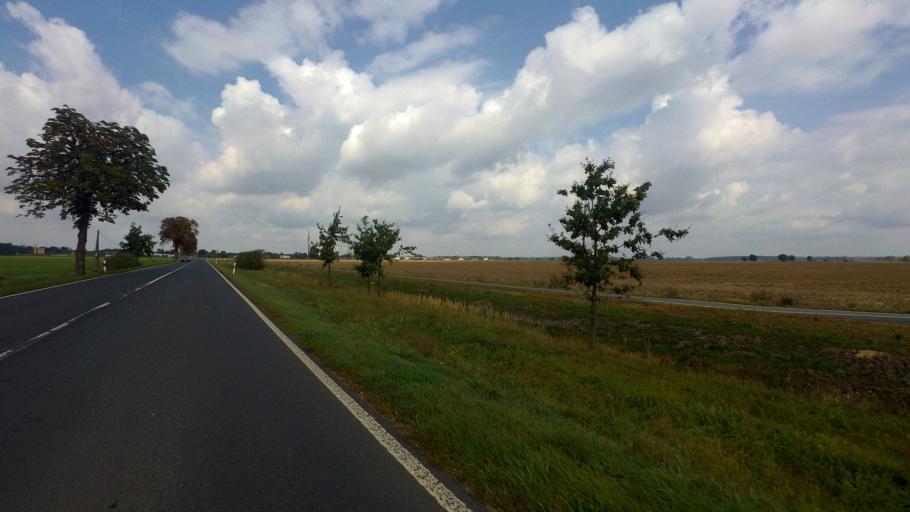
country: DE
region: Brandenburg
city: Herzberg
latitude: 51.6819
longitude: 13.2607
